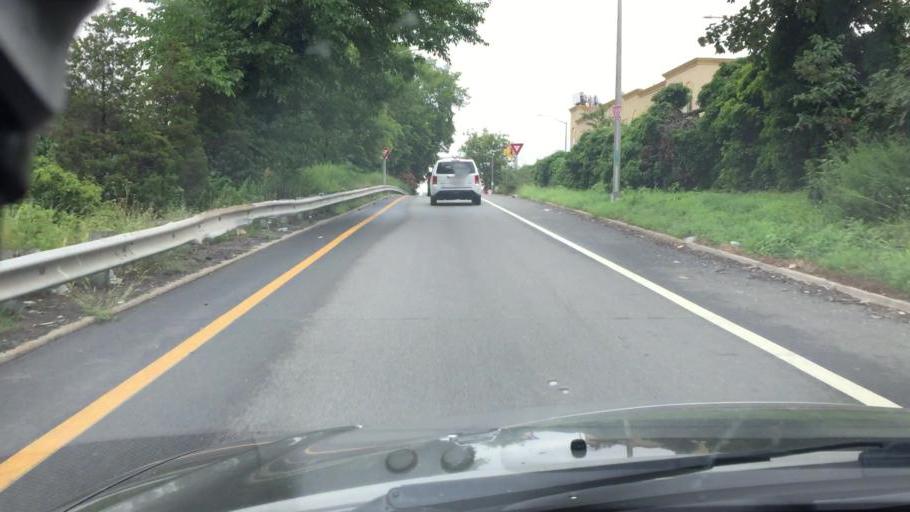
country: US
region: New York
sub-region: Queens County
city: Jamaica
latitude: 40.6844
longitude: -73.8068
